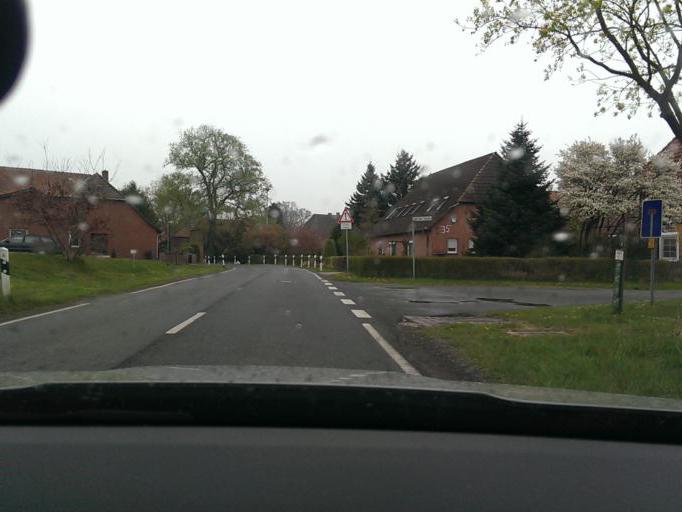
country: DE
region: Lower Saxony
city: Steimbke
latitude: 52.6188
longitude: 9.4861
